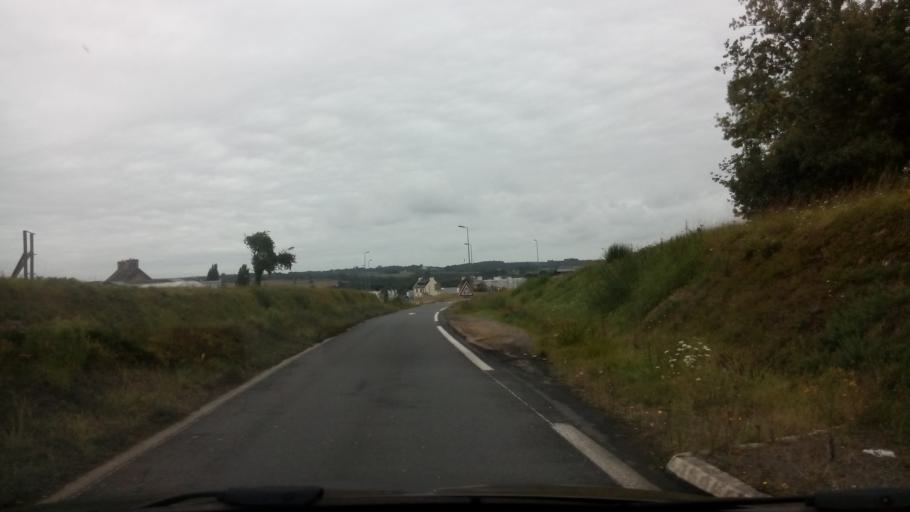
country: FR
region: Brittany
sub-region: Departement du Finistere
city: Morlaix
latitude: 48.5916
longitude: -3.8186
